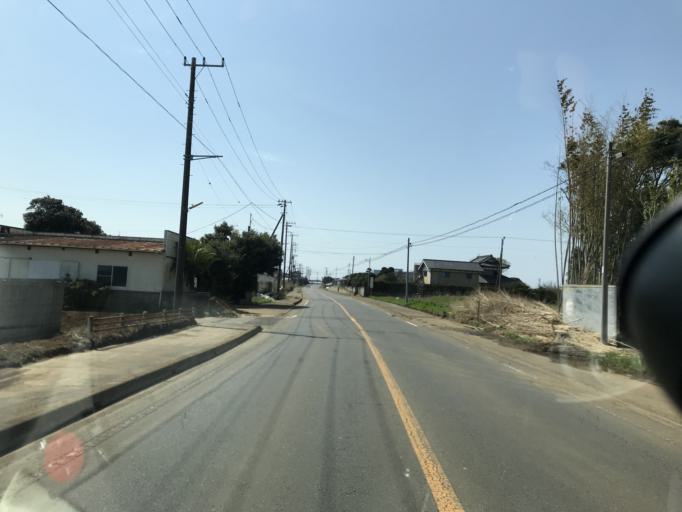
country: JP
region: Chiba
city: Asahi
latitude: 35.7909
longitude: 140.6963
